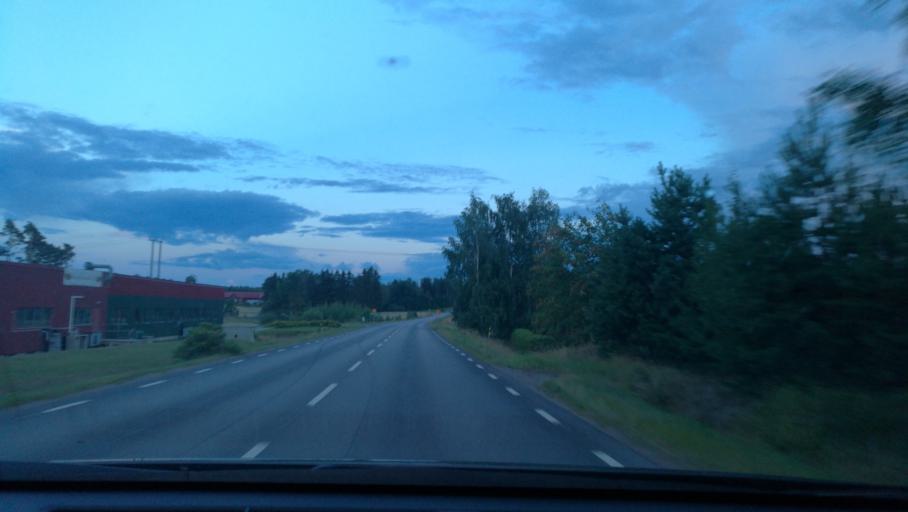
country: SE
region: OEstergoetland
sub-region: Norrkopings Kommun
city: Svartinge
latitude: 58.8235
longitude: 15.9421
